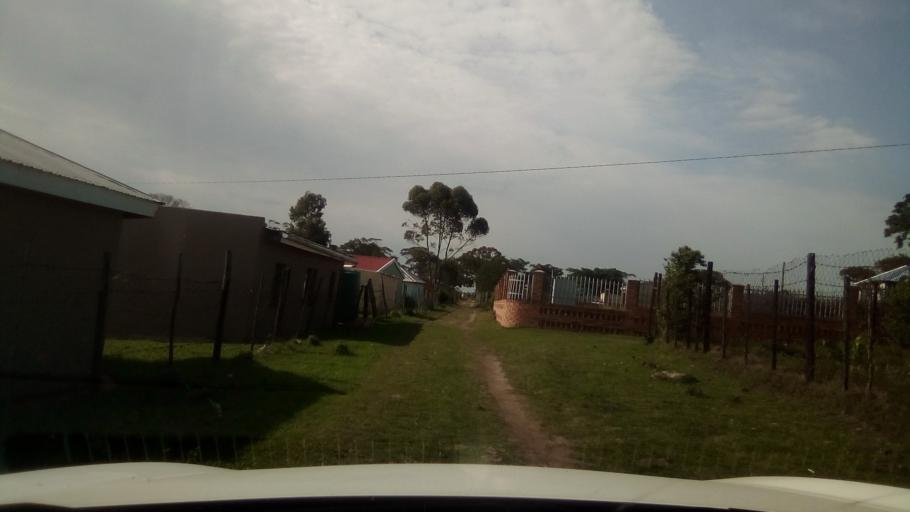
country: ZA
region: Eastern Cape
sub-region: Buffalo City Metropolitan Municipality
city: Bhisho
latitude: -32.9872
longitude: 27.2704
